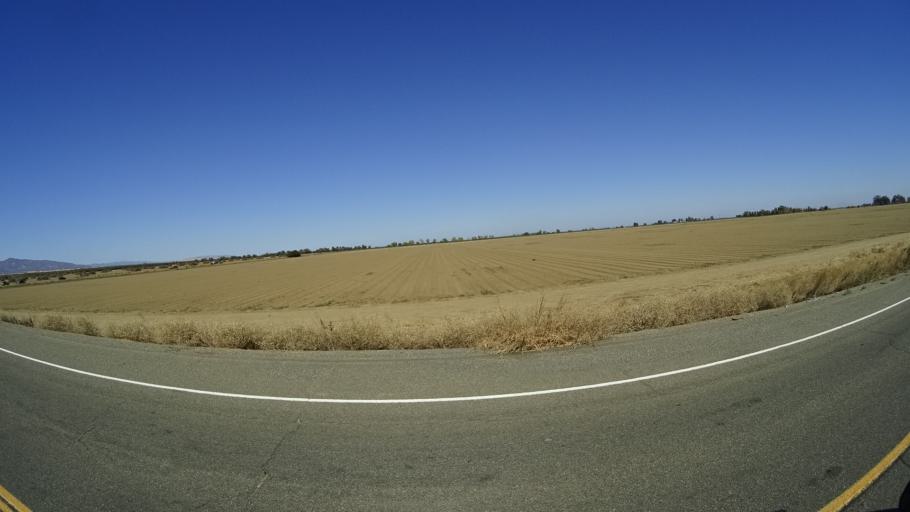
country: US
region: California
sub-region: Yolo County
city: Winters
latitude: 38.5617
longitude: -121.9509
